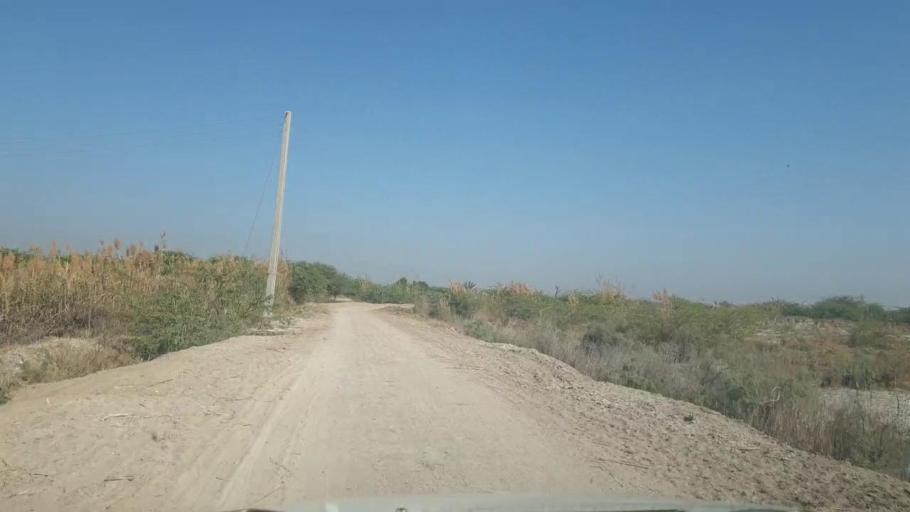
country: PK
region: Sindh
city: Mirpur Khas
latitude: 25.5154
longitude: 69.1492
